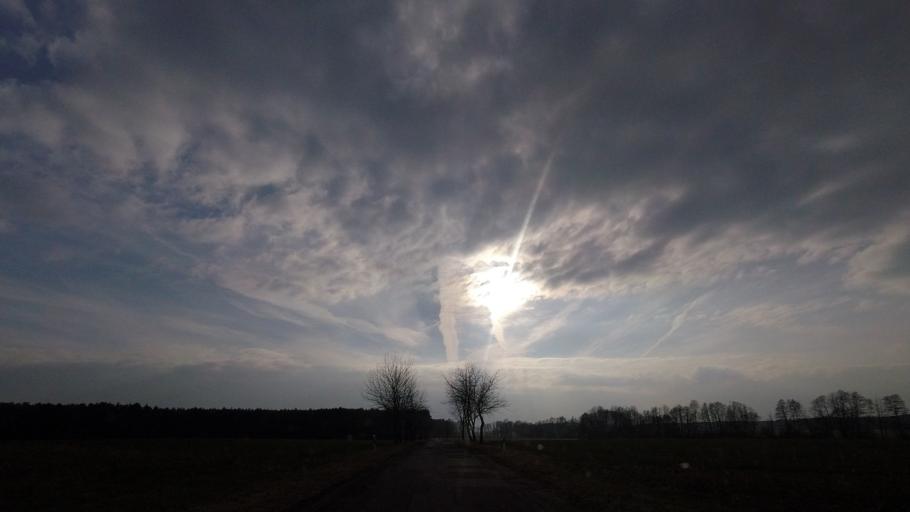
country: DE
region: Brandenburg
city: Belzig
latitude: 52.1620
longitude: 12.6766
